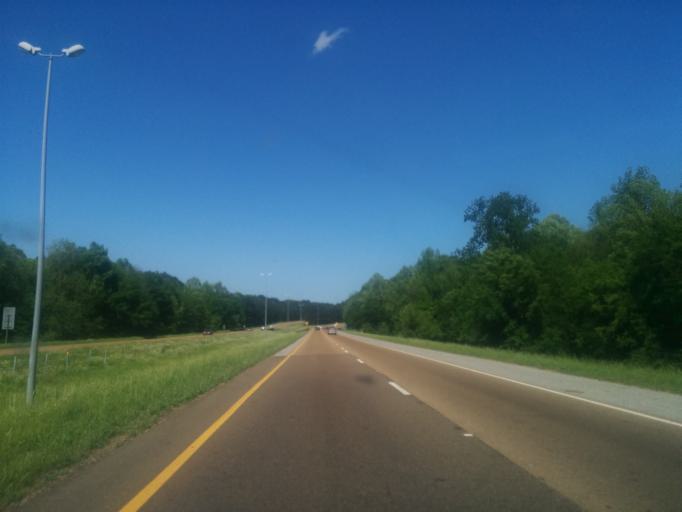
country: US
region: Mississippi
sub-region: Madison County
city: Ridgeland
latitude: 32.4090
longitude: -90.1641
